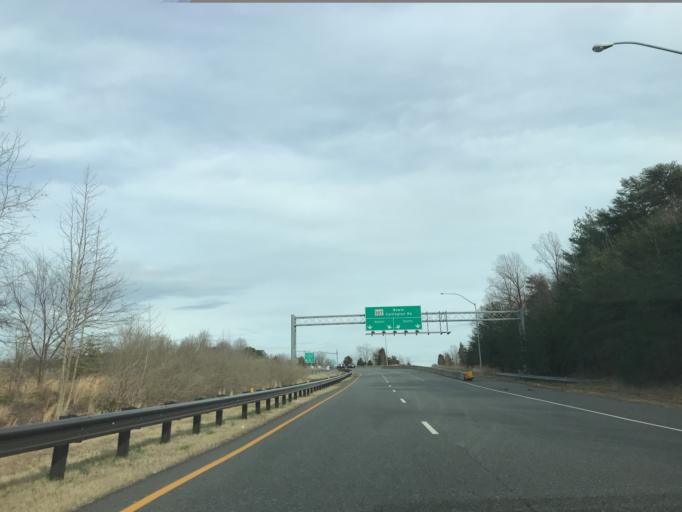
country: US
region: Maryland
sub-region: Prince George's County
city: Bowie
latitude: 38.9515
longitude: -76.7459
